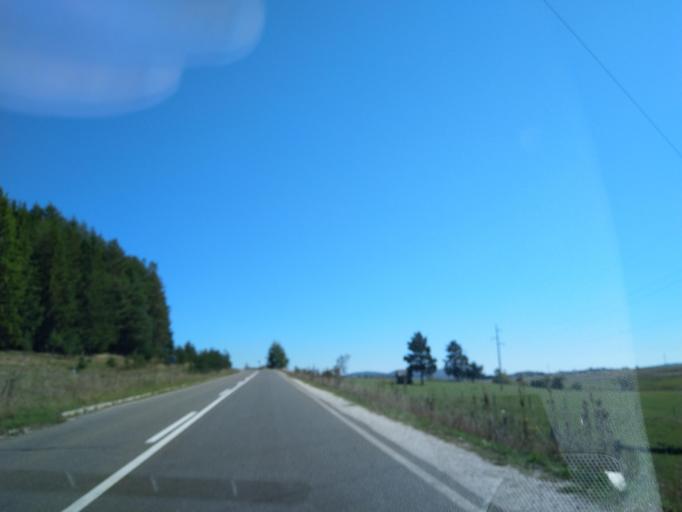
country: RS
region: Central Serbia
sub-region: Zlatiborski Okrug
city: Sjenica
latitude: 43.2688
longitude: 20.0264
